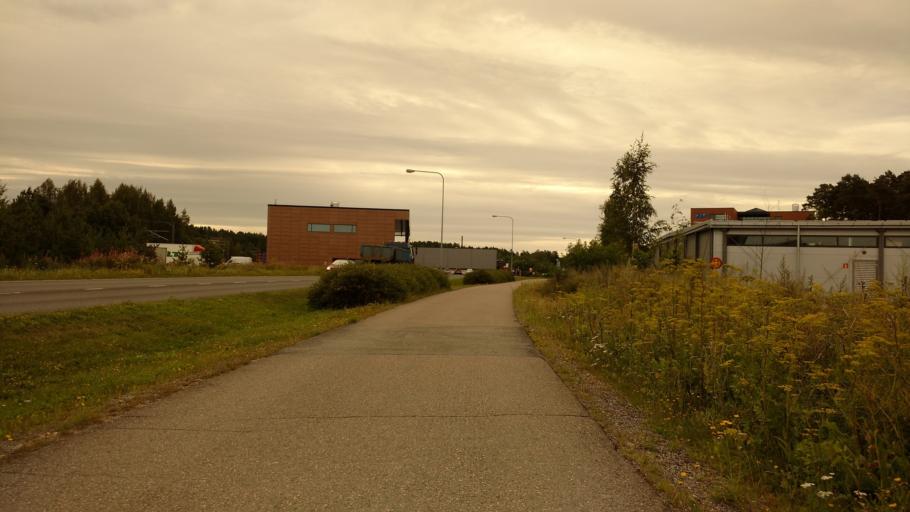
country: FI
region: Varsinais-Suomi
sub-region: Turku
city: Turku
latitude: 60.4405
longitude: 22.3163
